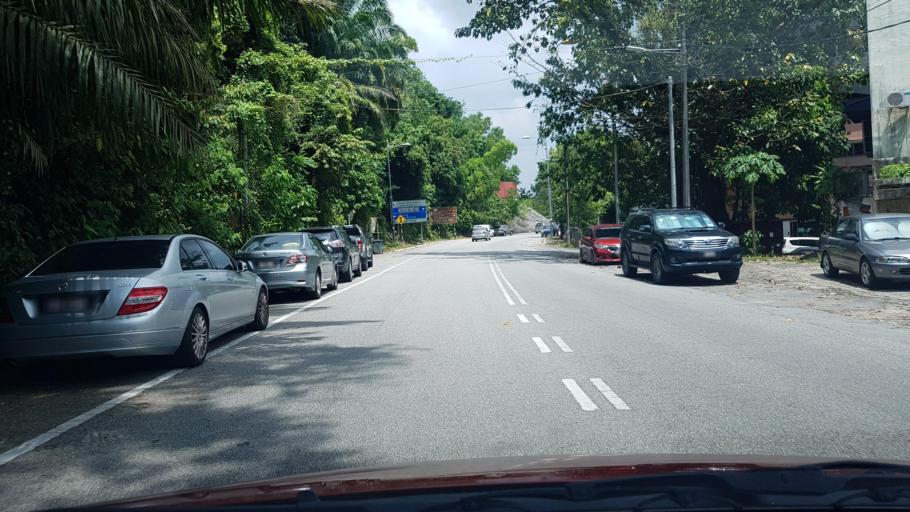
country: MY
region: Terengganu
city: Kuala Terengganu
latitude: 5.3259
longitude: 103.1338
